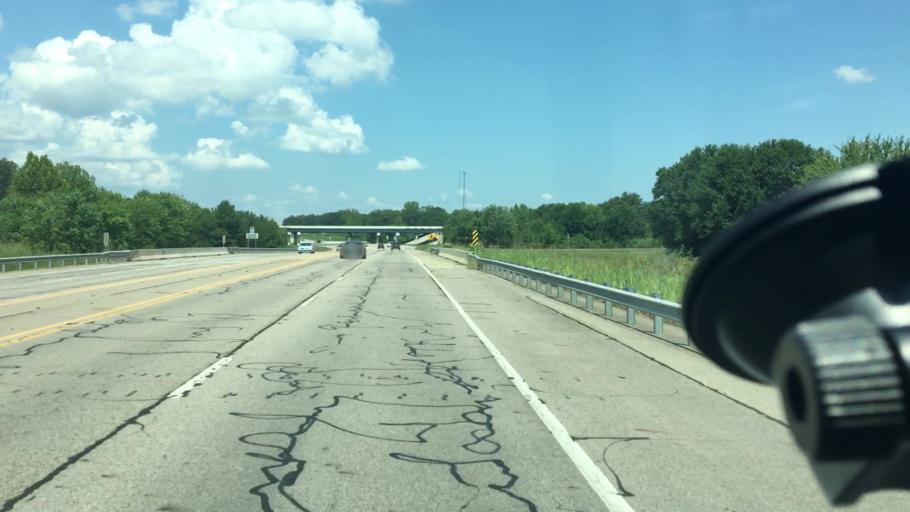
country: US
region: Arkansas
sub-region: Sebastian County
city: Barling
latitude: 35.3197
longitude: -94.2889
